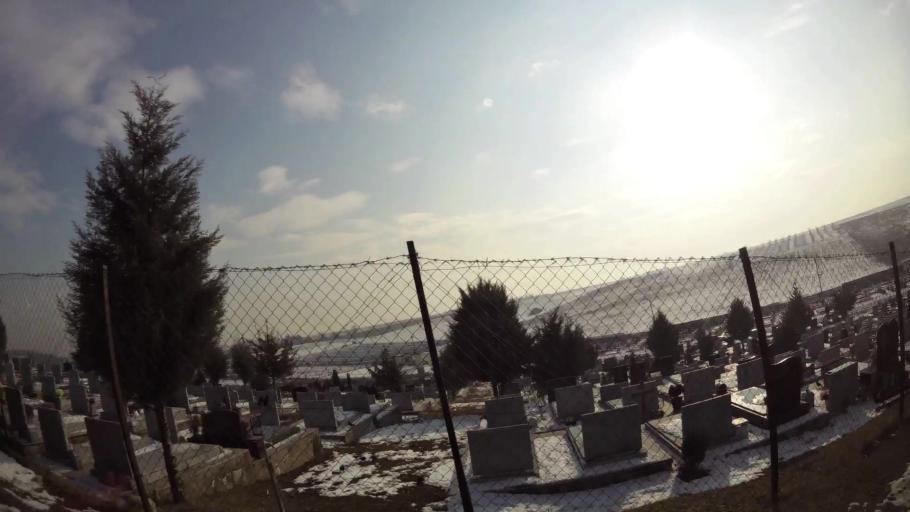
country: MK
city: Creshevo
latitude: 42.0158
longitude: 21.4918
